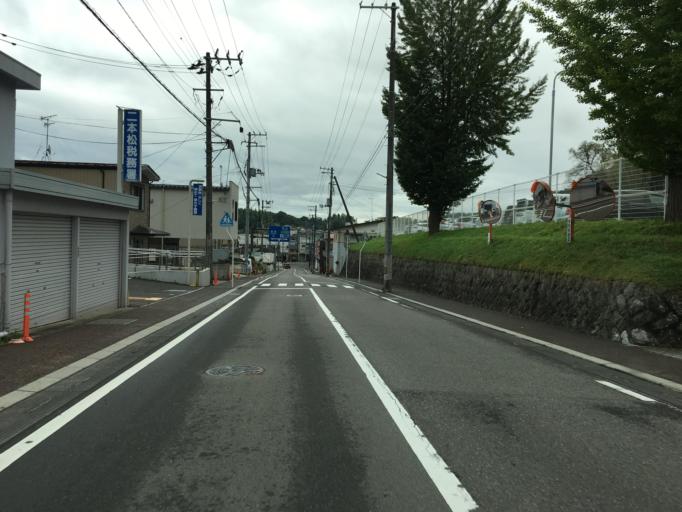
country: JP
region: Fukushima
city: Nihommatsu
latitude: 37.5937
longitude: 140.4397
